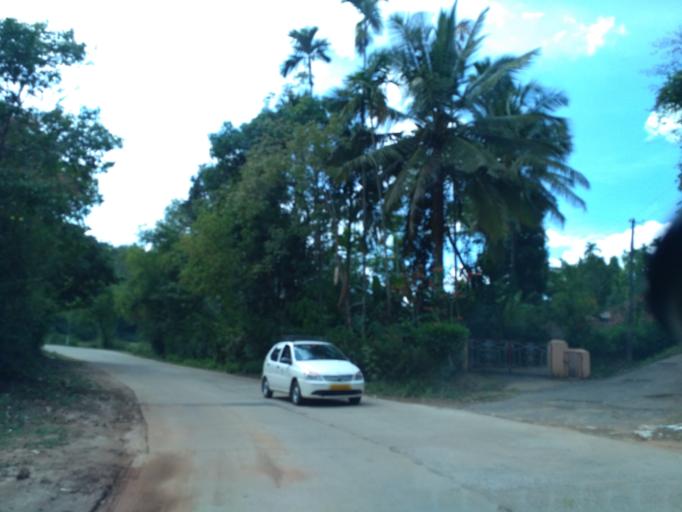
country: IN
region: Karnataka
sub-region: Kodagu
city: Madikeri
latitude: 12.3772
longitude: 75.7063
